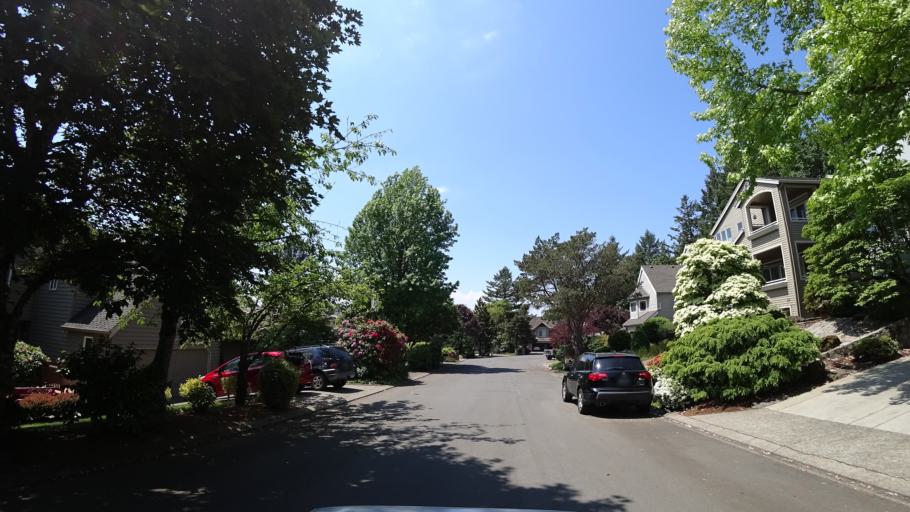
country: US
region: Oregon
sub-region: Washington County
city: Metzger
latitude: 45.4340
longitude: -122.7295
